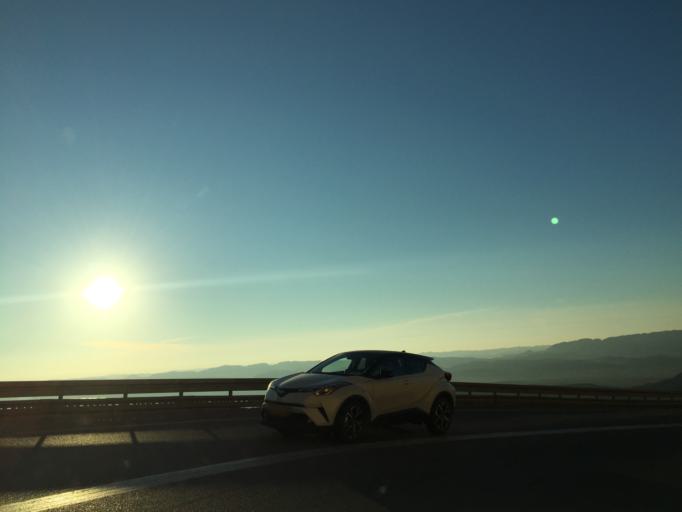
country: IL
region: Southern District
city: Mitzpe Ramon
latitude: 30.6234
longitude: 34.8178
